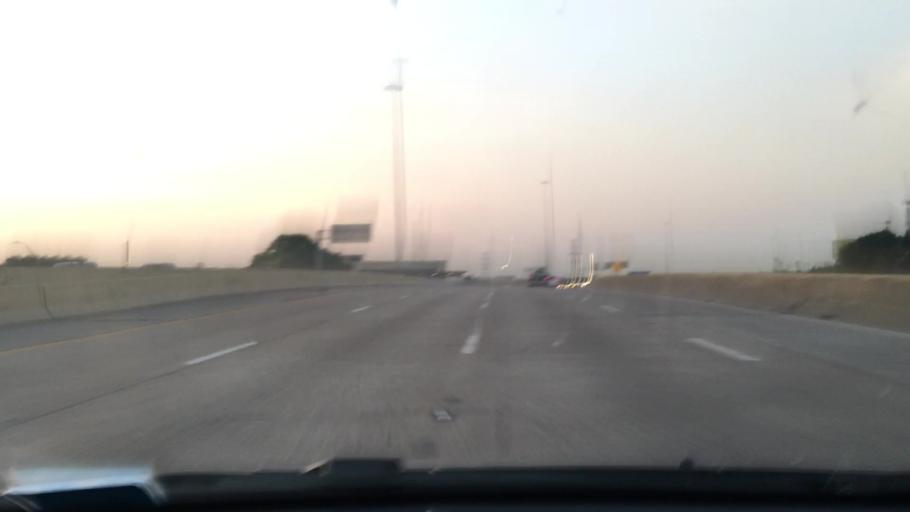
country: US
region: Texas
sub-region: Dallas County
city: Cockrell Hill
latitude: 32.7059
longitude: -96.8279
